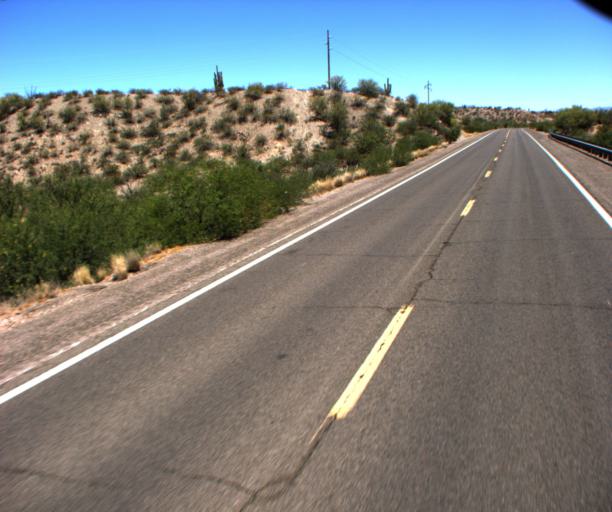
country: US
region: Arizona
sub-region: Pinal County
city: Kearny
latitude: 32.9674
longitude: -110.7577
